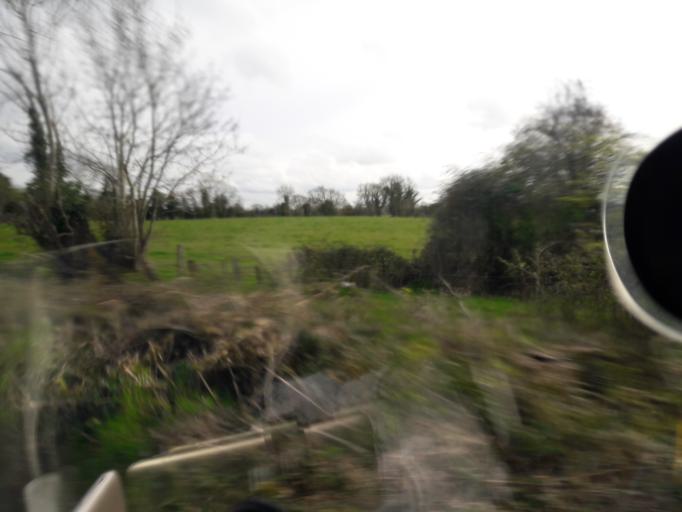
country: IE
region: Leinster
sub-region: An Mhi
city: Longwood
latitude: 53.4432
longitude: -6.9352
